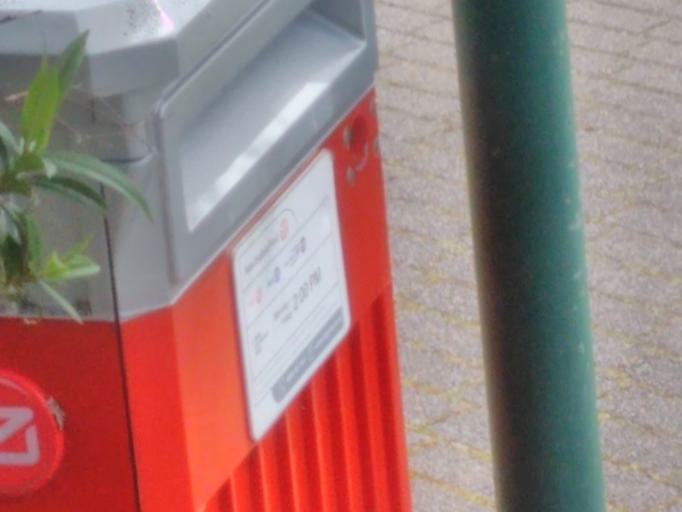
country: NZ
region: Manawatu-Wanganui
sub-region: Ruapehu District
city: Waiouru
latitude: -39.2009
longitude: 175.5395
